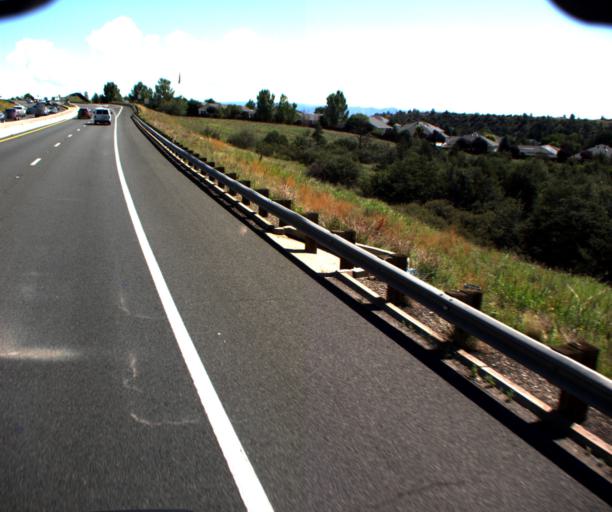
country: US
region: Arizona
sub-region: Yavapai County
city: Prescott Valley
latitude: 34.5696
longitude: -112.3712
